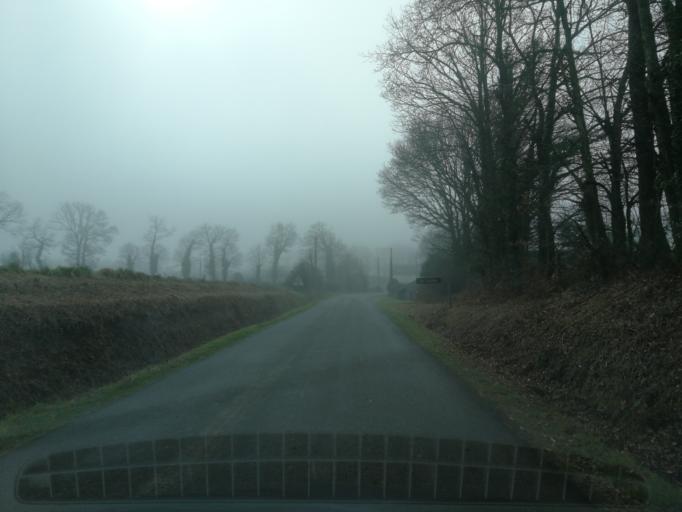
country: FR
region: Brittany
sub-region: Departement du Morbihan
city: La Vraie-Croix
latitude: 47.7274
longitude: -2.5091
